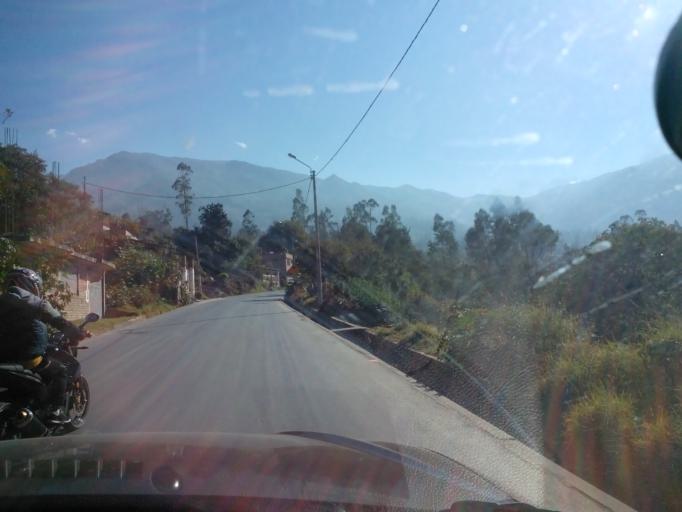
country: PE
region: Apurimac
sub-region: Provincia de Abancay
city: Tamburco
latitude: -13.6222
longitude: -72.8717
